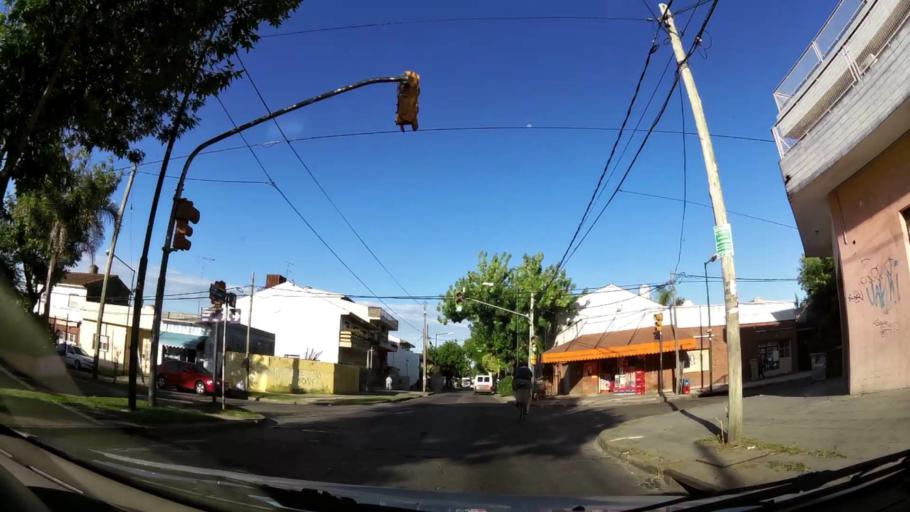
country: AR
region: Buenos Aires
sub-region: Partido de San Isidro
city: San Isidro
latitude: -34.4704
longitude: -58.5466
